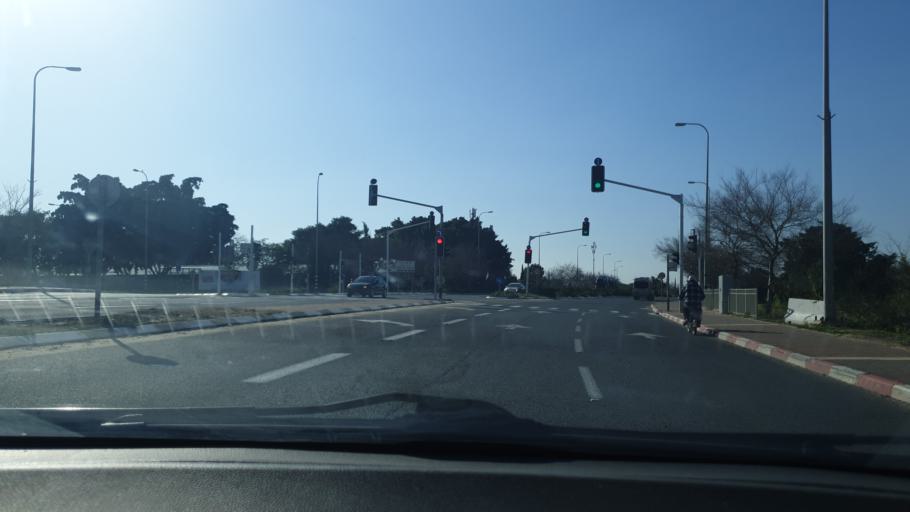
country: IL
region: Central District
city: Ness Ziona
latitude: 31.9437
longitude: 34.8261
